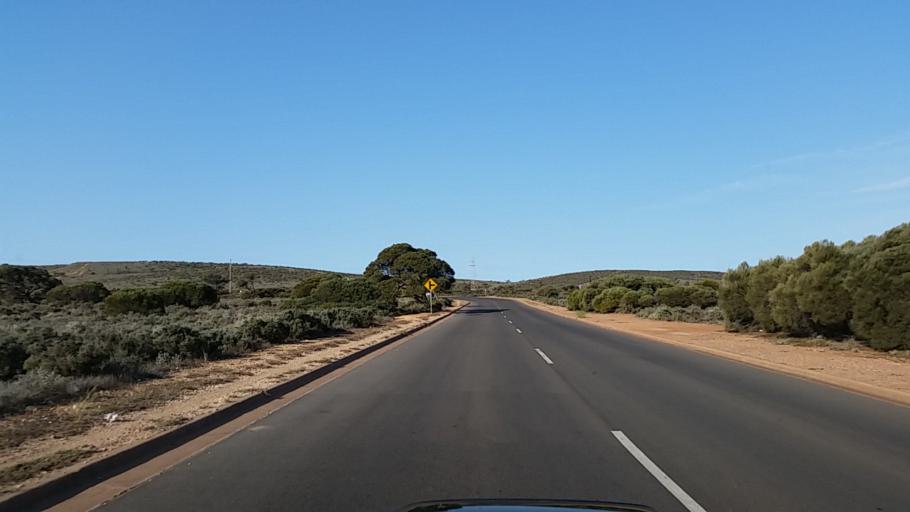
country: AU
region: South Australia
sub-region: Whyalla
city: Whyalla
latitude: -33.0090
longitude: 137.5294
